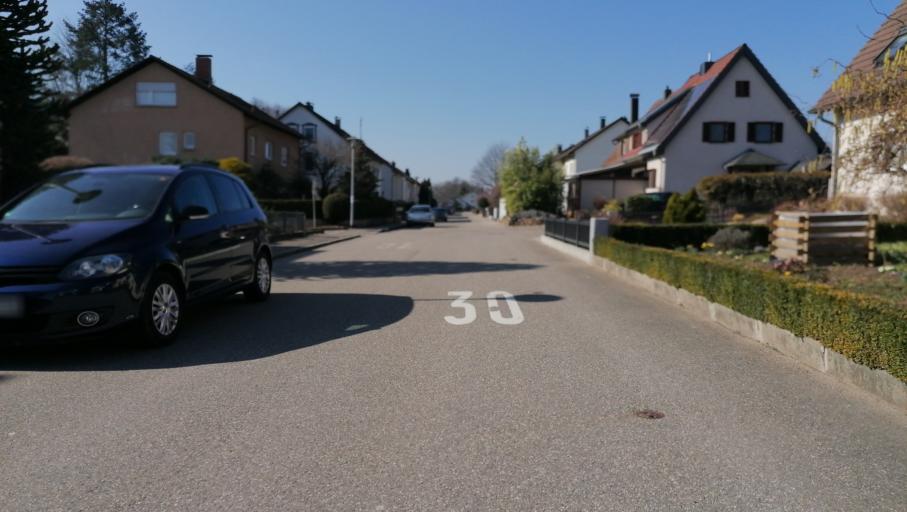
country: DE
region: Baden-Wuerttemberg
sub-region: Freiburg Region
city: Bad Sackingen
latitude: 47.5589
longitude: 7.9355
